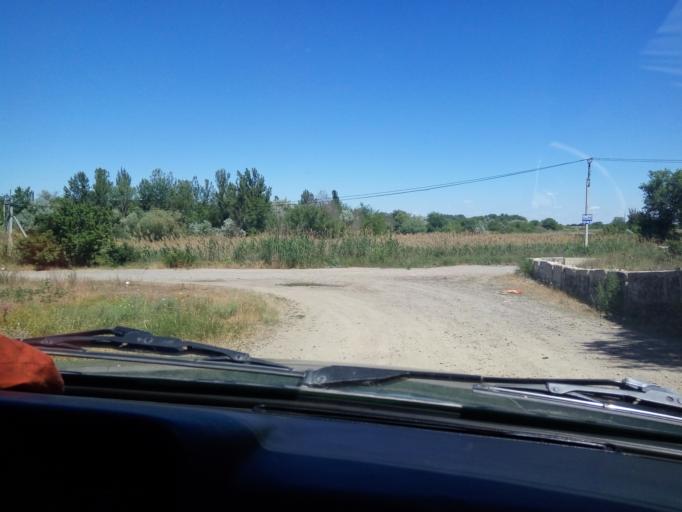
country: RU
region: Rostov
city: Bataysk
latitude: 47.0831
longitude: 39.7486
